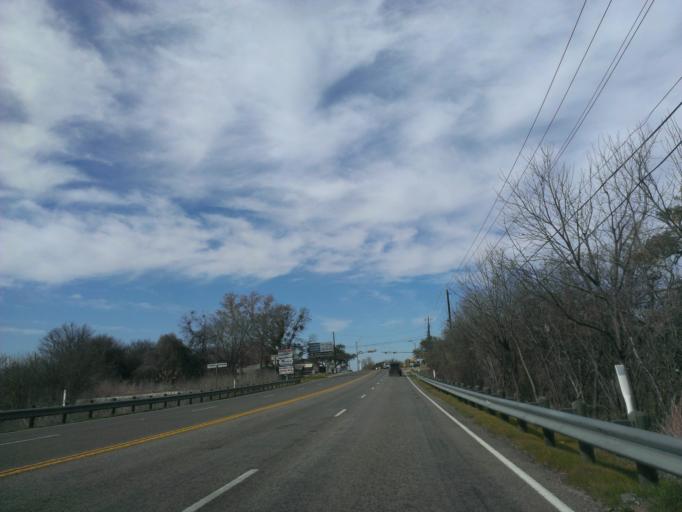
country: US
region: Texas
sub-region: Llano County
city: Kingsland
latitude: 30.6560
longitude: -98.4240
